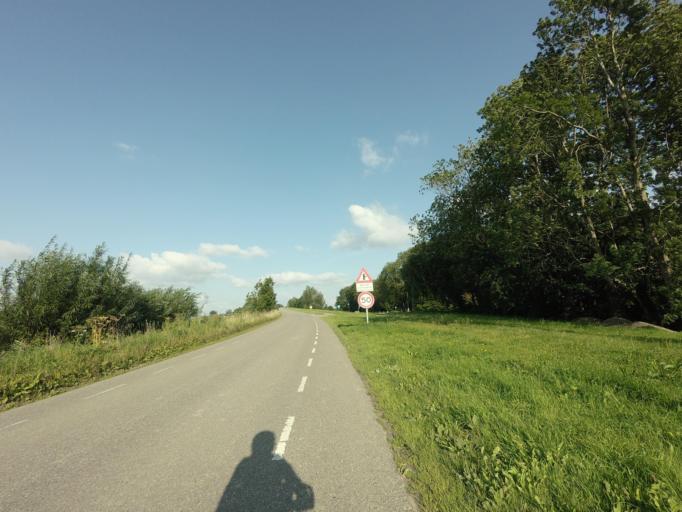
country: NL
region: Flevoland
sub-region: Gemeente Noordoostpolder
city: Ens
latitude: 52.6677
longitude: 5.7869
